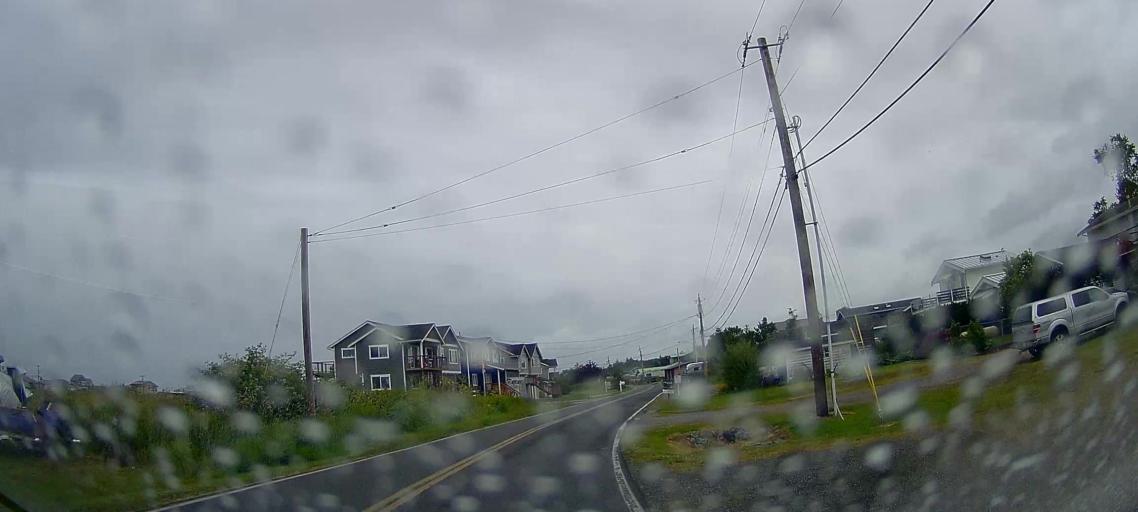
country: US
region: Washington
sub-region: Whatcom County
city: Birch Bay
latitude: 48.7997
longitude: -122.7073
